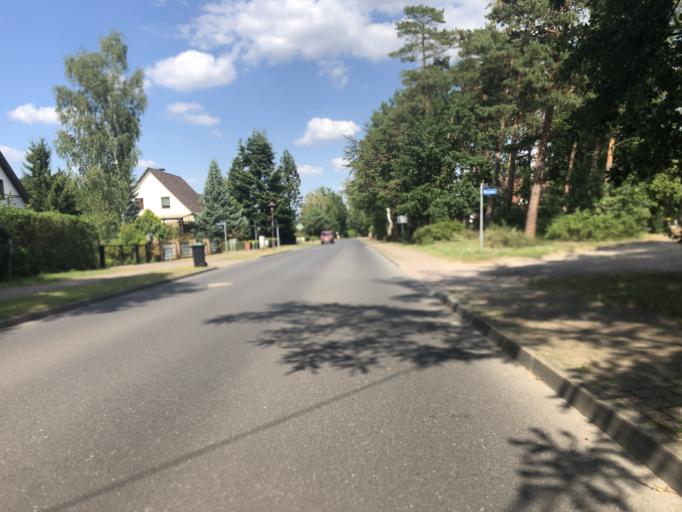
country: DE
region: Brandenburg
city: Mullrose
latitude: 52.2322
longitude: 14.4133
